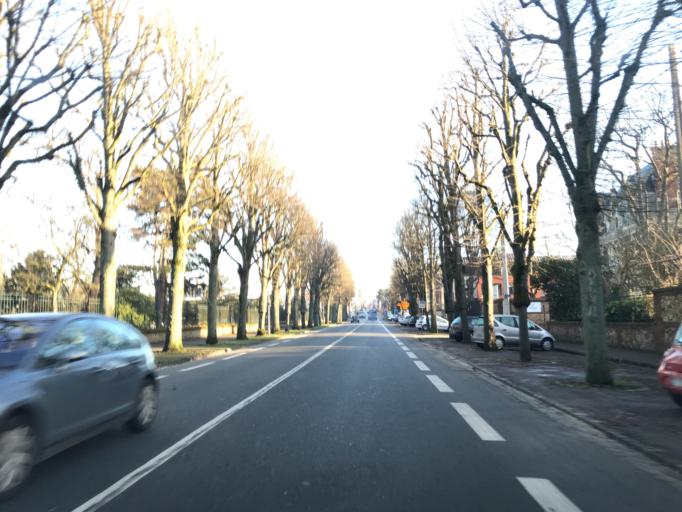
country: FR
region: Haute-Normandie
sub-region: Departement de la Seine-Maritime
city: Sotteville-les-Rouen
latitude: 49.4202
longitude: 1.0787
